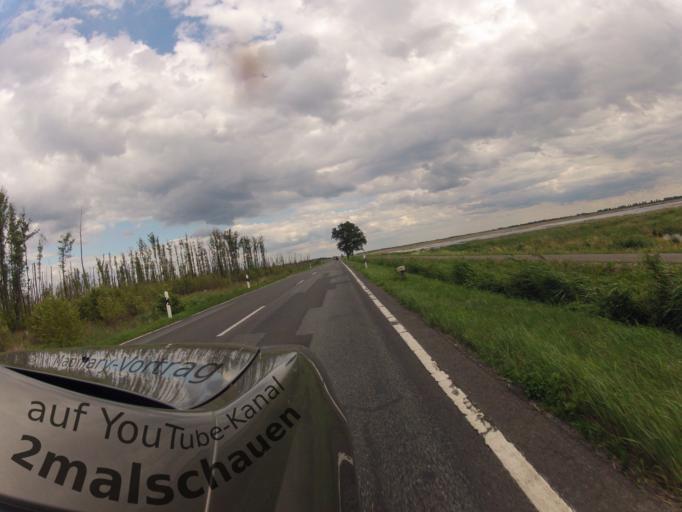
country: DE
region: Mecklenburg-Vorpommern
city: Lassan
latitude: 53.8763
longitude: 13.8032
